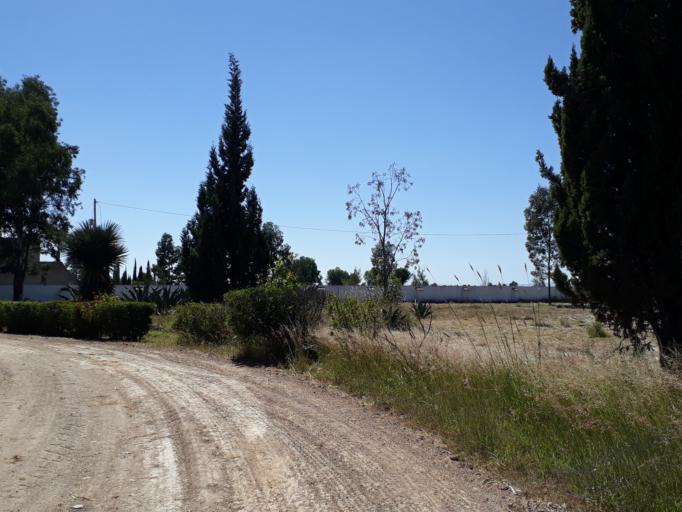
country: MX
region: Aguascalientes
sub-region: Aguascalientes
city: Penuelas (El Cienegal)
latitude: 21.7592
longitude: -102.2799
